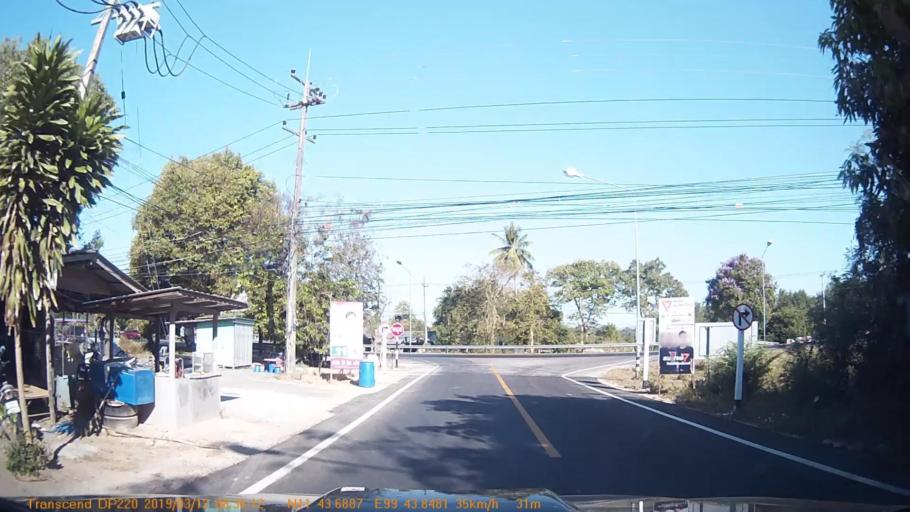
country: TH
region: Prachuap Khiri Khan
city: Prachuap Khiri Khan
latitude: 11.7282
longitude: 99.7307
